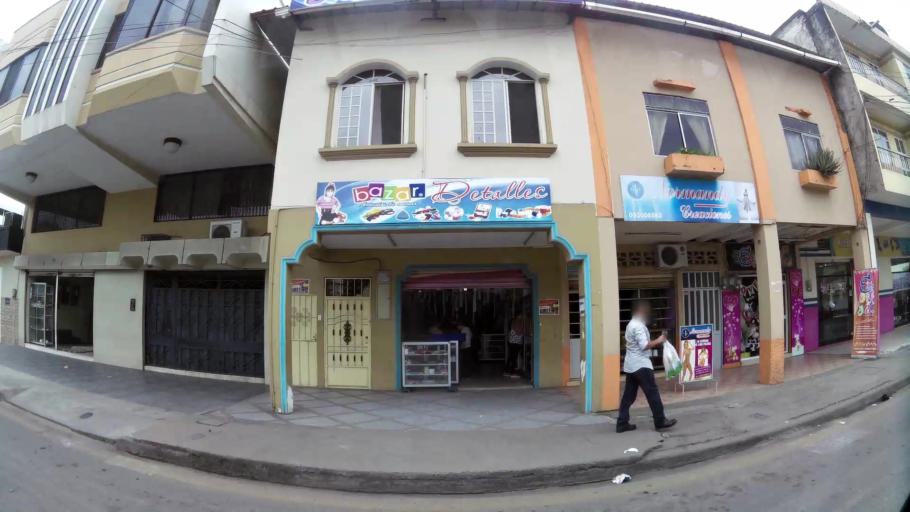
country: EC
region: El Oro
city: Machala
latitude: -3.2561
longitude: -79.9605
